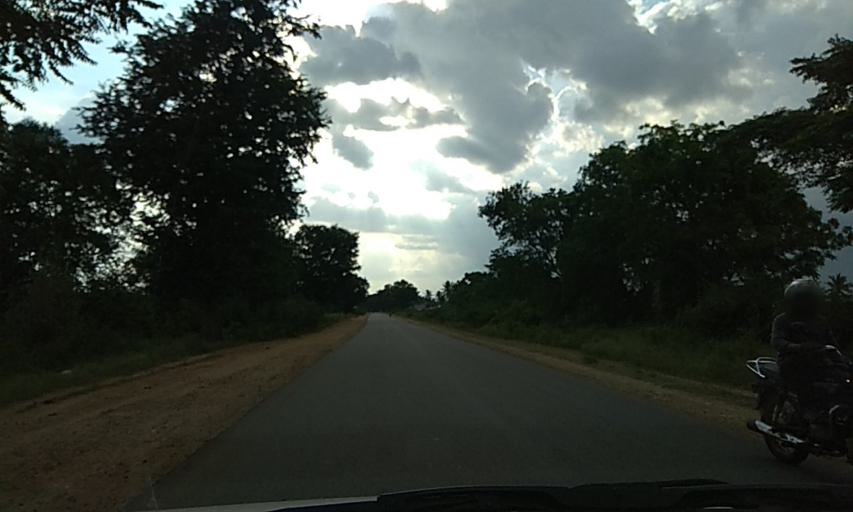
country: IN
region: Karnataka
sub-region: Chamrajnagar
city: Gundlupet
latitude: 11.8110
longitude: 76.7321
